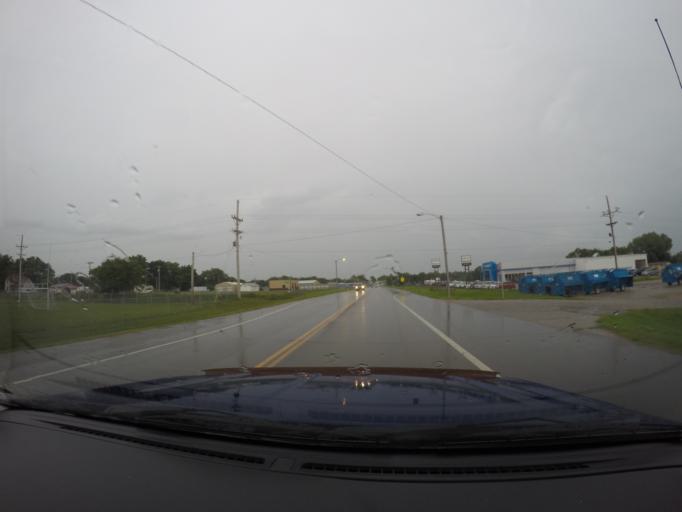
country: US
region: Kansas
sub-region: Cloud County
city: Concordia
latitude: 39.5716
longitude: -97.6410
